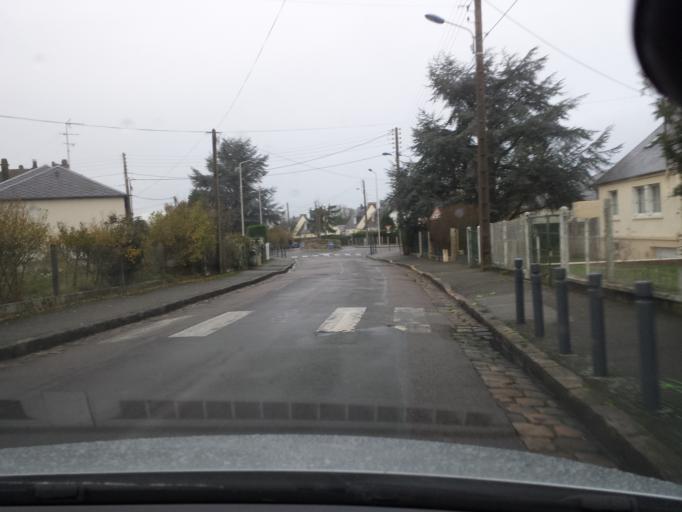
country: FR
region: Haute-Normandie
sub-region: Departement de l'Eure
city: Evreux
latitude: 49.0138
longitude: 1.1536
